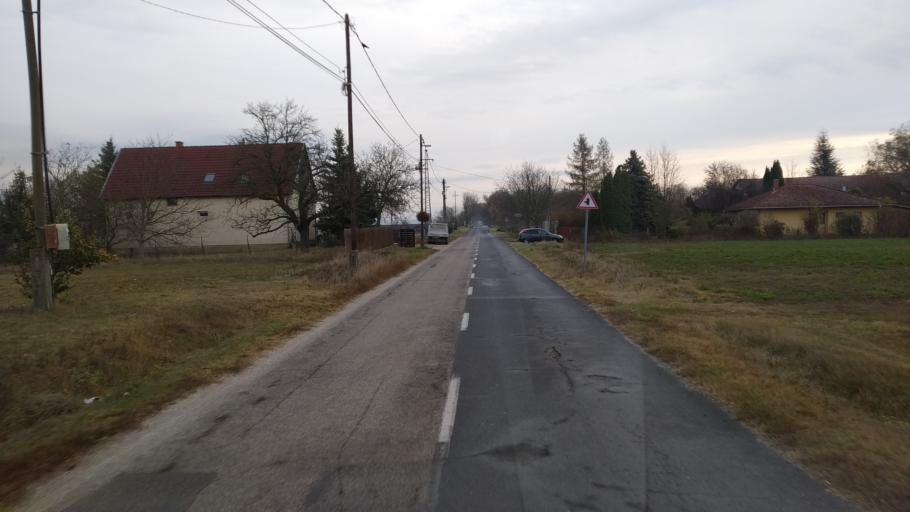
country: HU
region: Pest
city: Veroce
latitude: 47.8051
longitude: 19.0197
